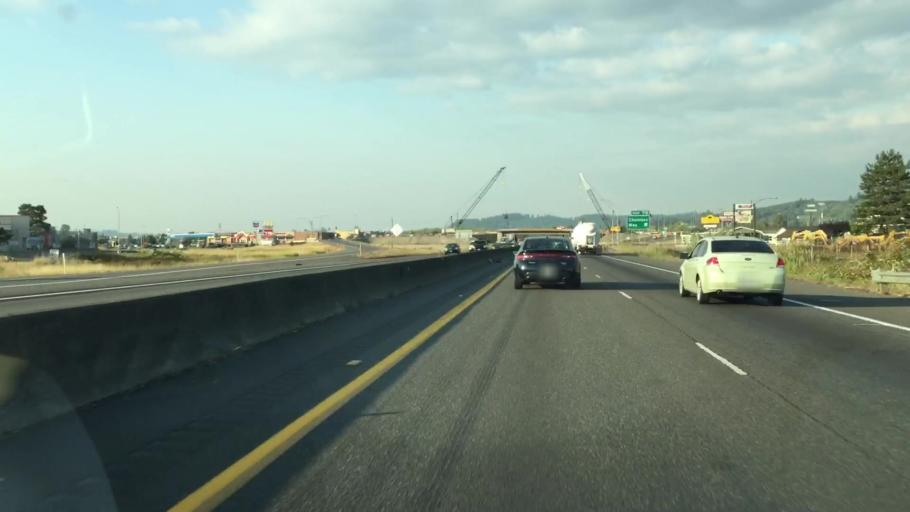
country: US
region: Washington
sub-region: Lewis County
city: Chehalis
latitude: 46.6724
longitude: -122.9772
